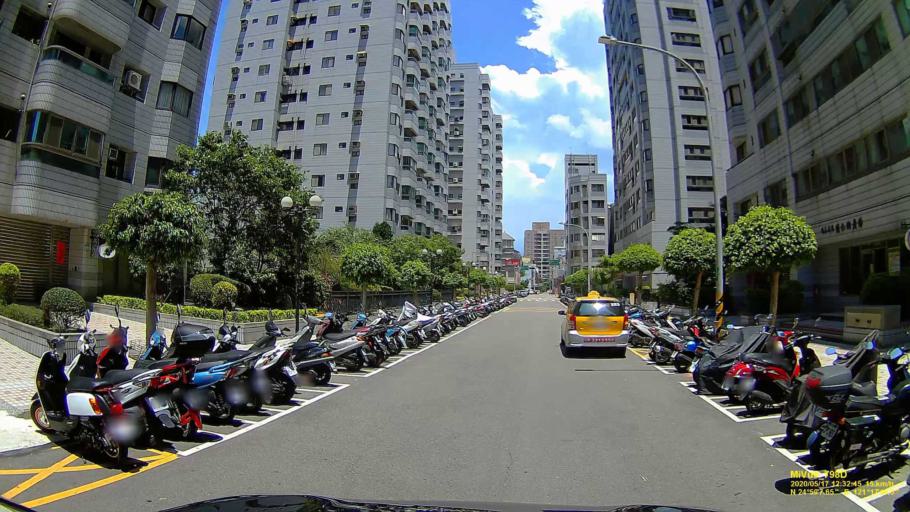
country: TW
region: Taiwan
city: Taoyuan City
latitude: 24.9855
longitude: 121.2877
